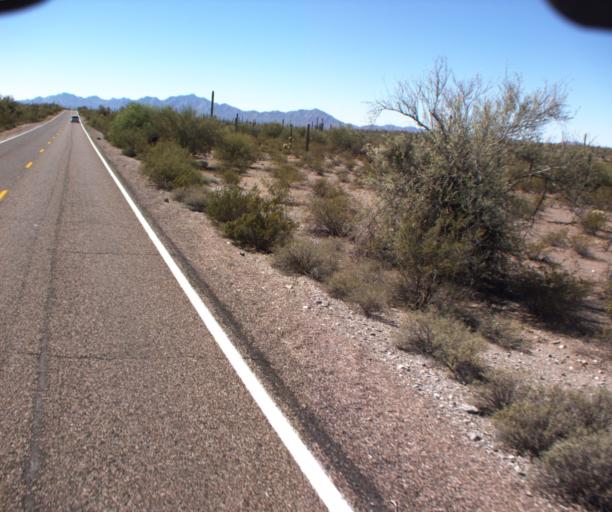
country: MX
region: Sonora
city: Sonoyta
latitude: 31.9458
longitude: -112.7992
